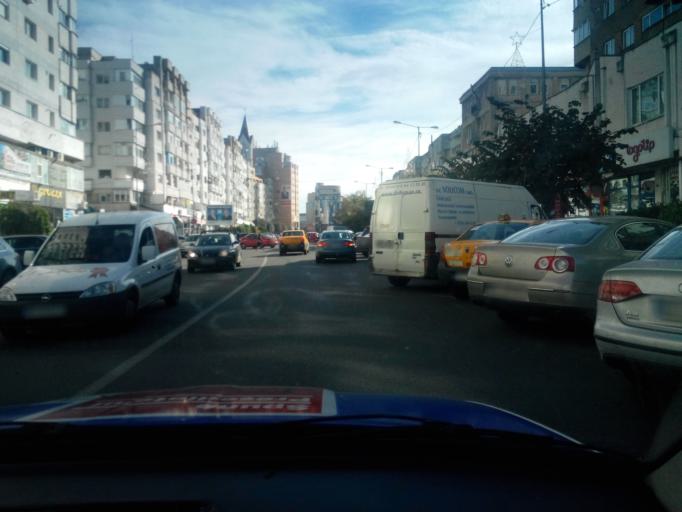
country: RO
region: Bacau
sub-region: Municipiul Bacau
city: Bacau
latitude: 46.5679
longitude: 26.9126
